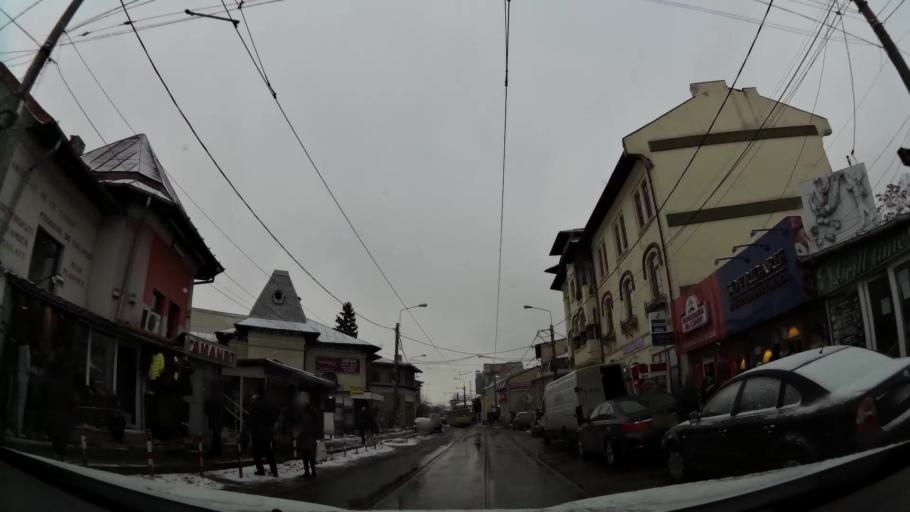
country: RO
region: Prahova
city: Ploiesti
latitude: 44.9442
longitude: 26.0236
